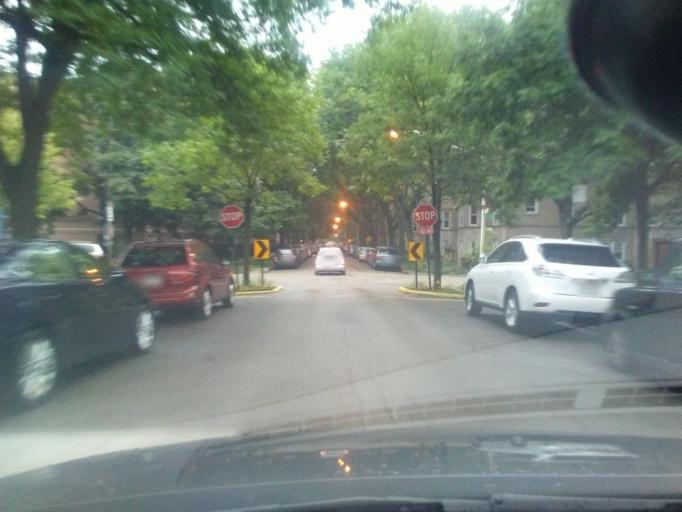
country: US
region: Illinois
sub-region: Cook County
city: Evanston
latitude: 41.9908
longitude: -87.6680
